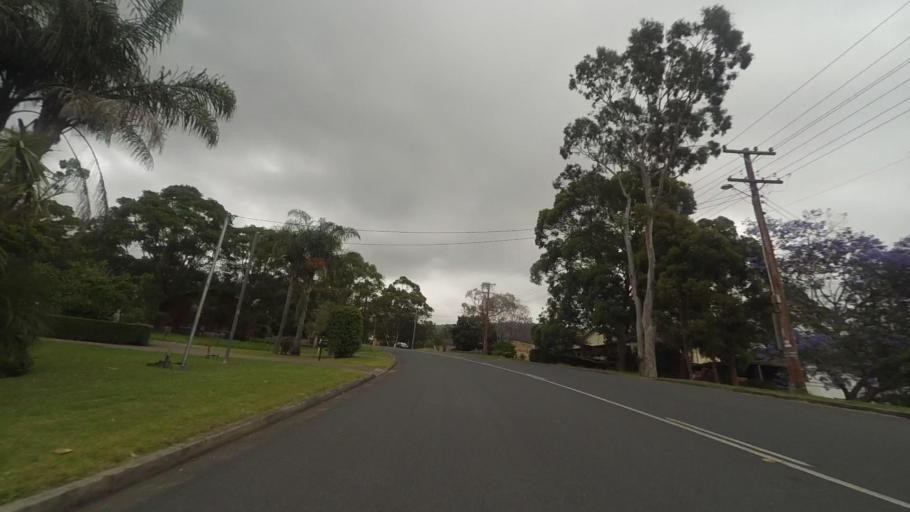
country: AU
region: New South Wales
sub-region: Wollongong
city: Cordeaux Heights
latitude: -34.4307
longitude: 150.8277
